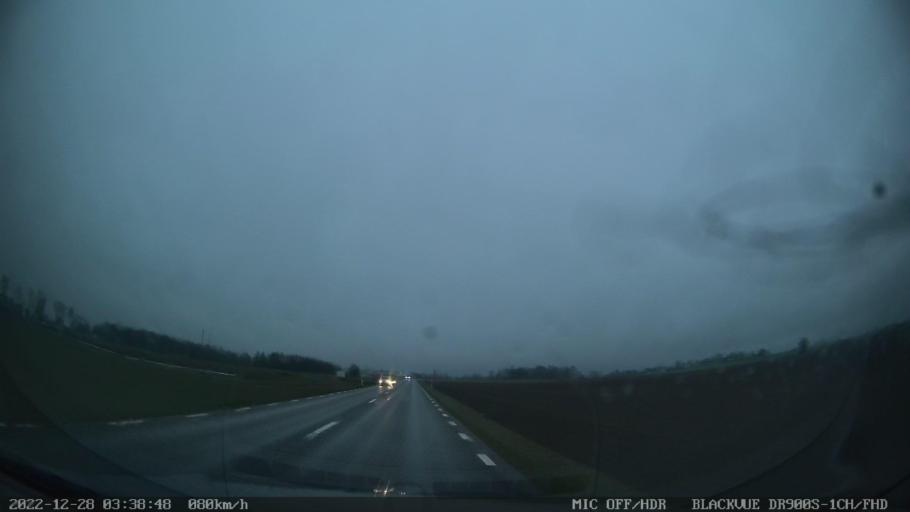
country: SE
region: Skane
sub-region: Tomelilla Kommun
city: Tomelilla
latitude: 55.5469
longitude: 14.0564
